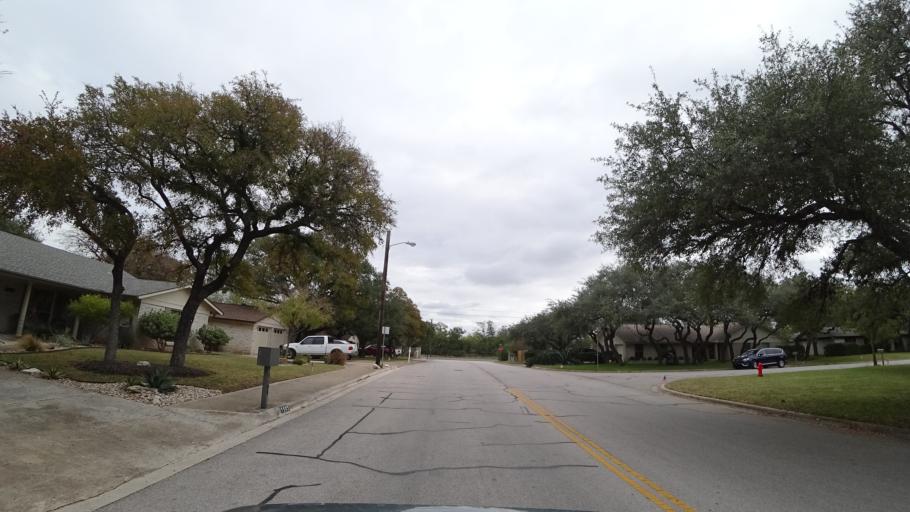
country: US
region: Texas
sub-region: Williamson County
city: Round Rock
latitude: 30.4921
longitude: -97.6952
